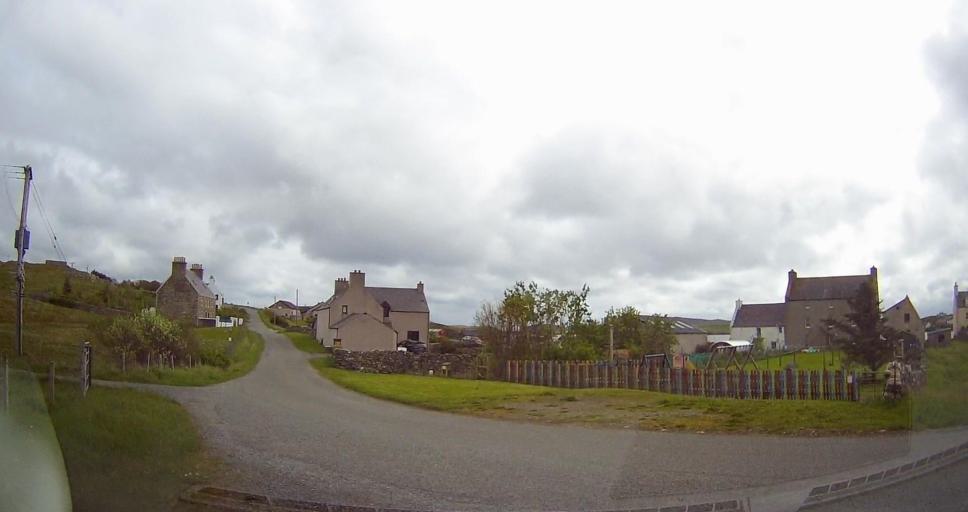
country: GB
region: Scotland
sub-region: Shetland Islands
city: Sandwick
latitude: 60.2285
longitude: -1.5624
